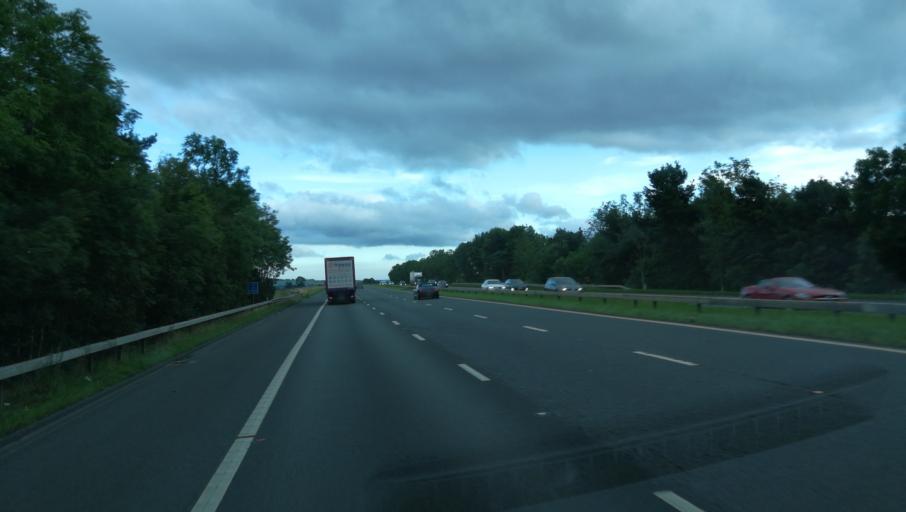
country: GB
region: England
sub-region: Cumbria
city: Penrith
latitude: 54.7435
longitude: -2.8102
